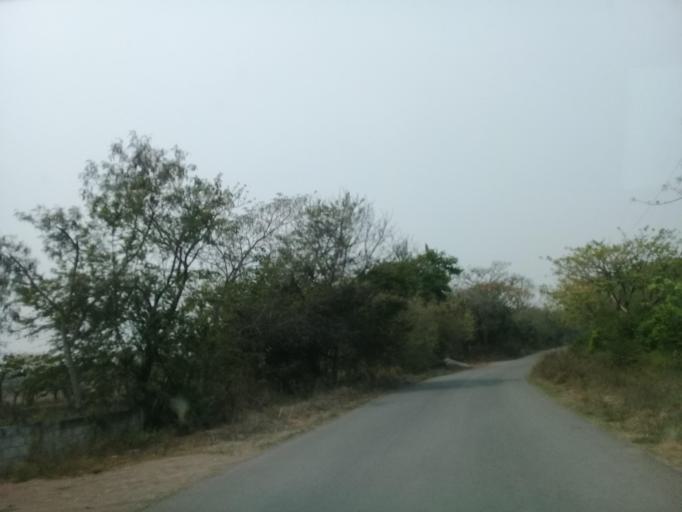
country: MX
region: Veracruz
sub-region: Medellin
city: La Laguna y Monte del Castillo
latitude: 18.9485
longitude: -96.1266
